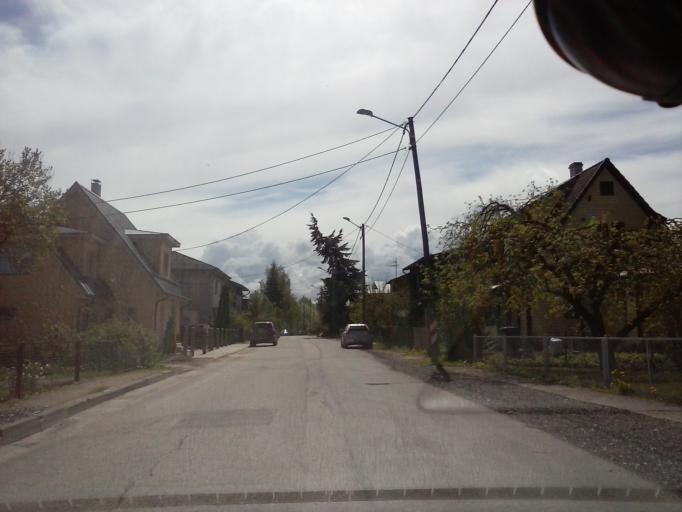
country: EE
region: Tartu
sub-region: Tartu linn
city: Tartu
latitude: 58.3530
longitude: 26.7180
